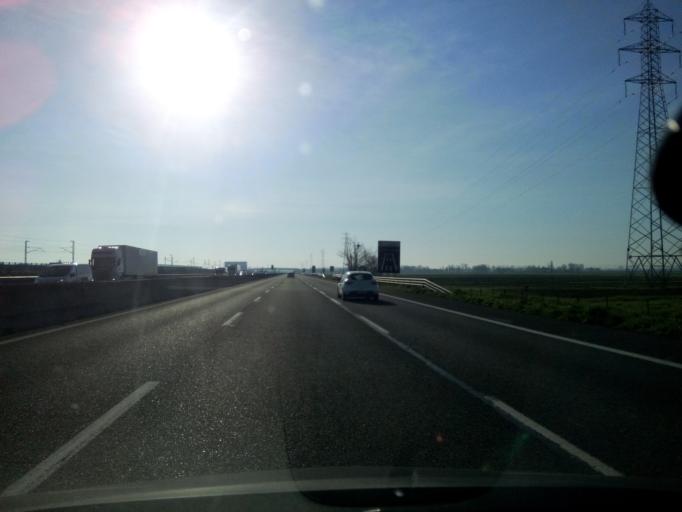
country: IT
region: Emilia-Romagna
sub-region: Provincia di Reggio Emilia
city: Prato
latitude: 44.7012
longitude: 10.7475
